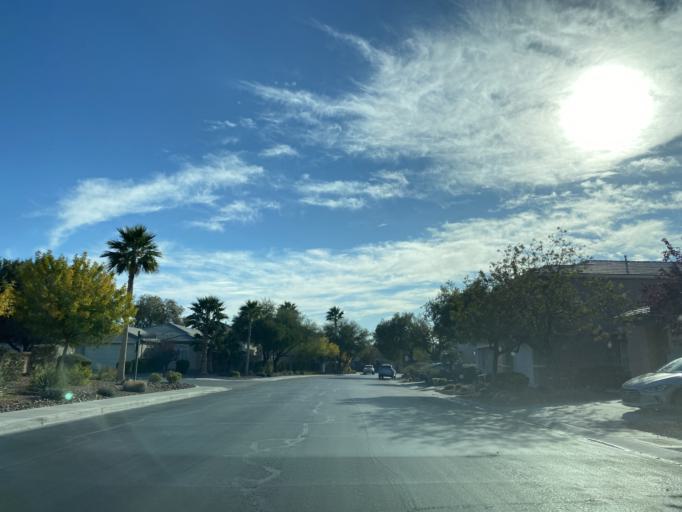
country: US
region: Nevada
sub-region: Clark County
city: North Las Vegas
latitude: 36.3166
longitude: -115.2437
